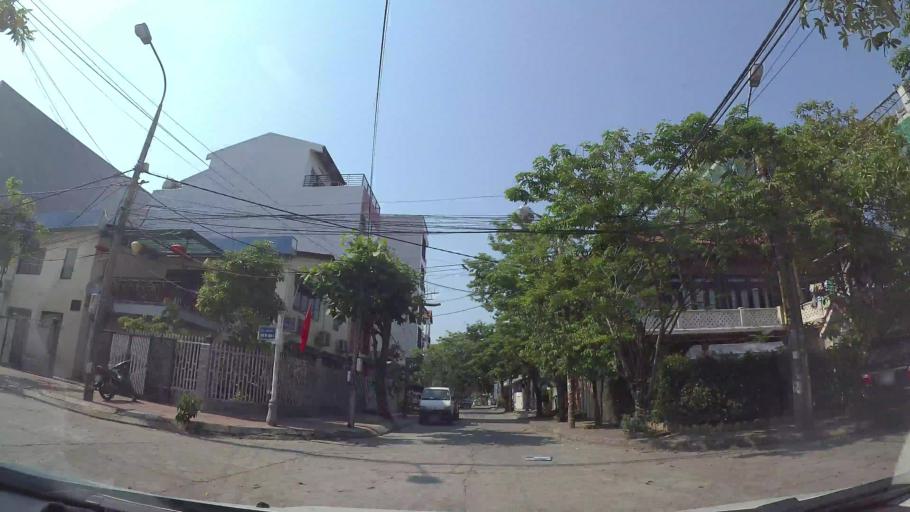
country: VN
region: Da Nang
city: Ngu Hanh Son
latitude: 16.0386
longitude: 108.2464
